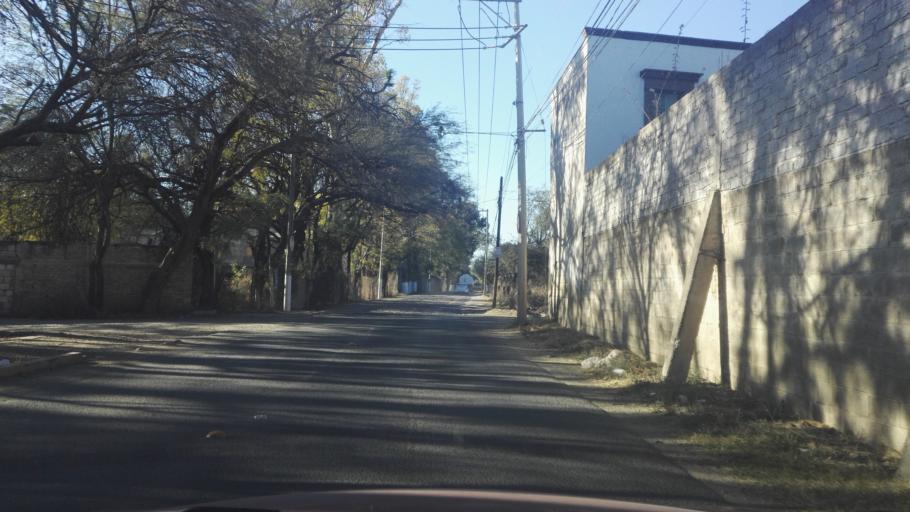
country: MX
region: Guanajuato
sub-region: Leon
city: Ladrilleras del Refugio
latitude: 21.0685
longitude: -101.5979
